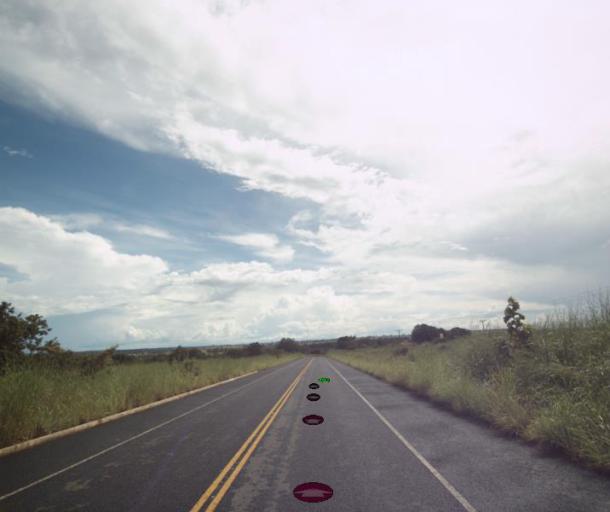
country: BR
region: Goias
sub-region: Sao Miguel Do Araguaia
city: Sao Miguel do Araguaia
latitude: -13.3021
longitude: -50.2658
